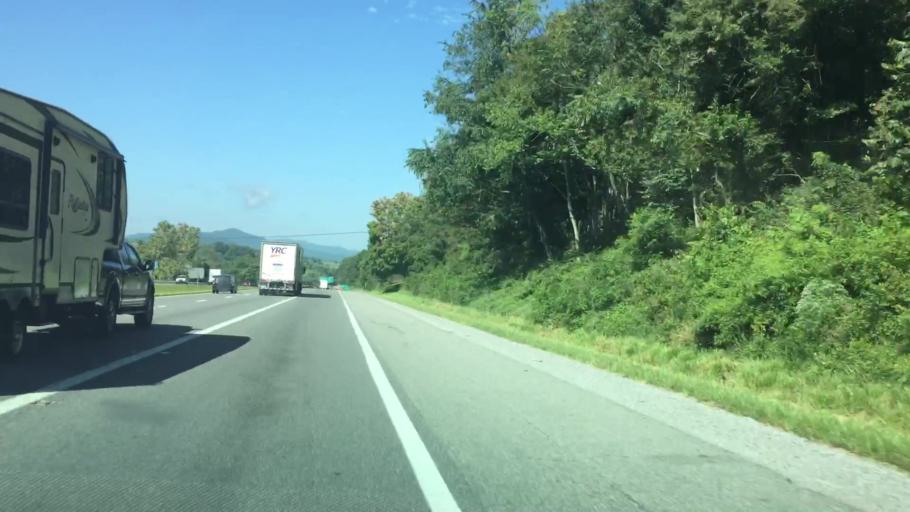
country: US
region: Virginia
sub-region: Pulaski County
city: Pulaski
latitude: 36.9486
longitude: -80.8851
